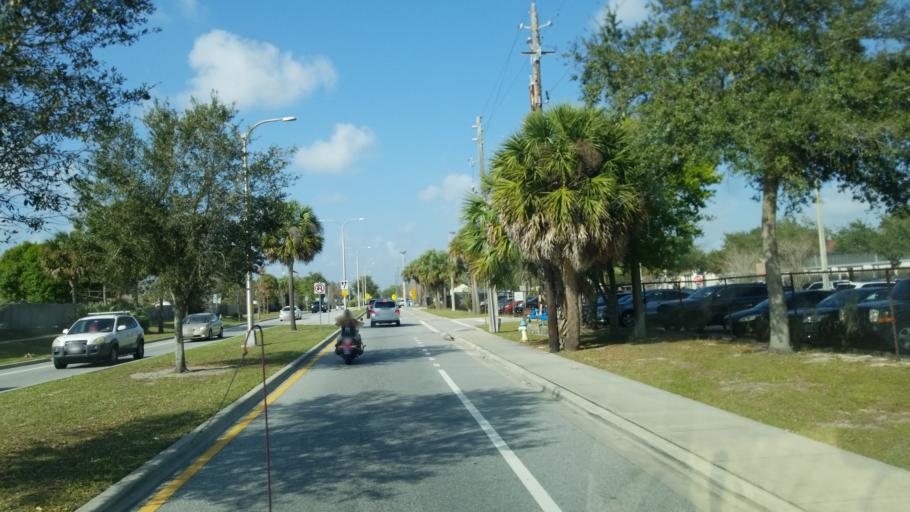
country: US
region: Florida
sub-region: Sarasota County
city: Fruitville
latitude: 27.3305
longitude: -82.4638
